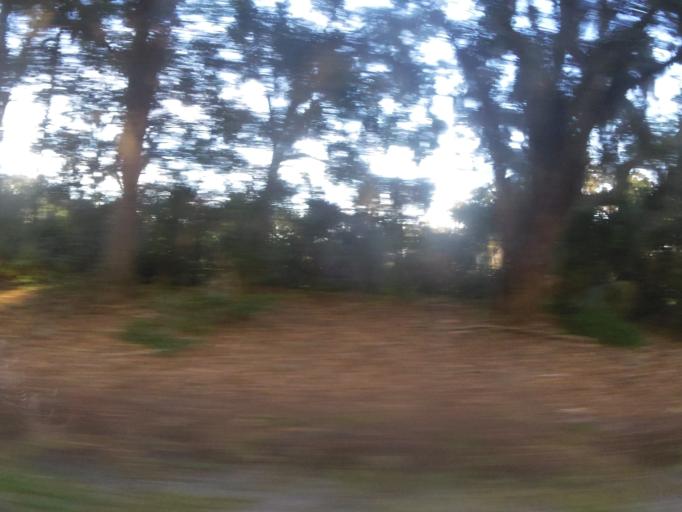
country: US
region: Florida
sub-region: Saint Johns County
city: Palm Valley
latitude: 30.1556
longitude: -81.3813
